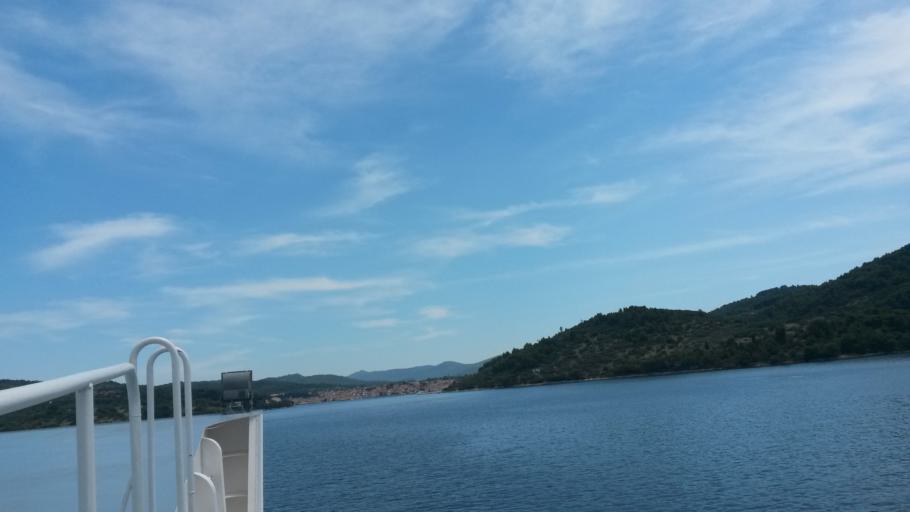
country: HR
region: Dubrovacko-Neretvanska
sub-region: Grad Dubrovnik
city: Vela Luka
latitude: 42.9633
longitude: 16.6889
